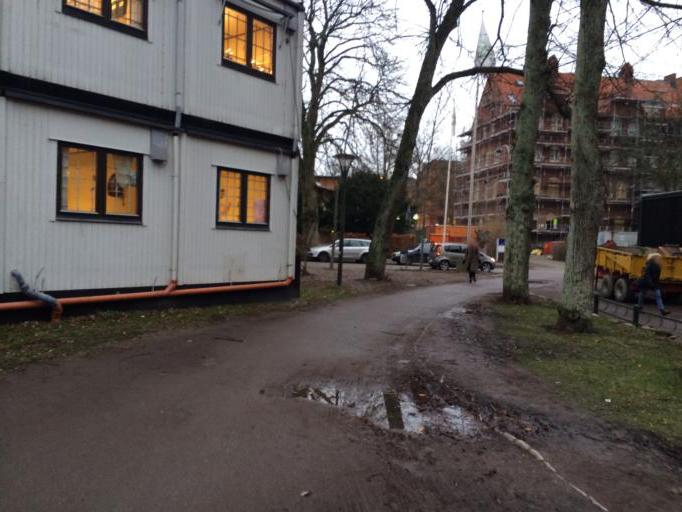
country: SE
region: Skane
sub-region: Lunds Kommun
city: Lund
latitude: 55.7092
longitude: 13.1986
